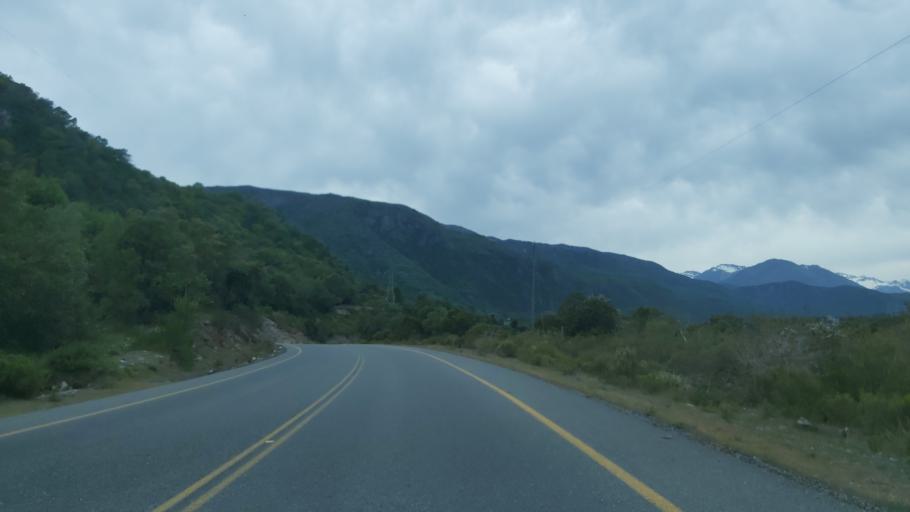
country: CL
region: Maule
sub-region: Provincia de Linares
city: Colbun
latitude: -35.7161
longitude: -71.0393
